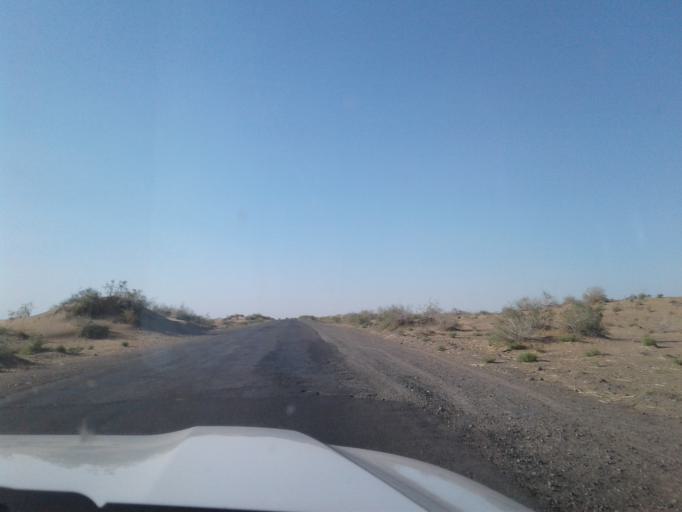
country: TM
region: Mary
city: Yoloeten
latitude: 37.0169
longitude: 62.4570
